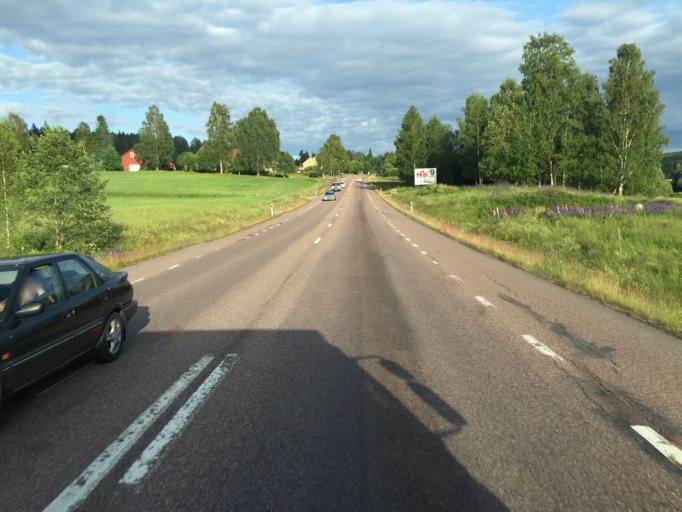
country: SE
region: Dalarna
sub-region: Borlange Kommun
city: Borlaenge
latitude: 60.5358
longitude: 15.2933
